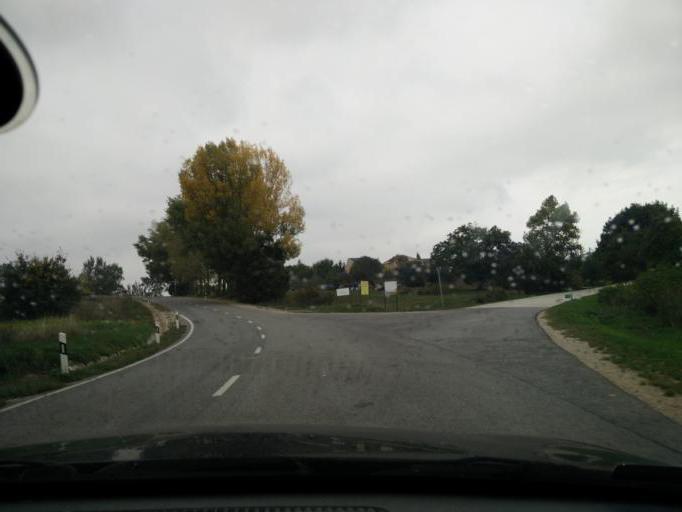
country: HU
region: Komarom-Esztergom
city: Bajna
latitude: 47.6581
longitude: 18.5880
